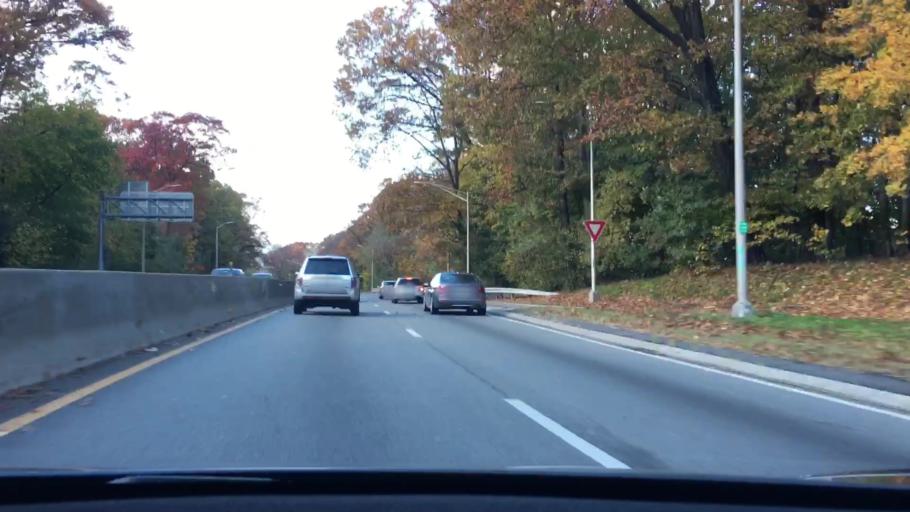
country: US
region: New York
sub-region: Queens County
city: Borough of Queens
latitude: 40.7025
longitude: -73.8610
